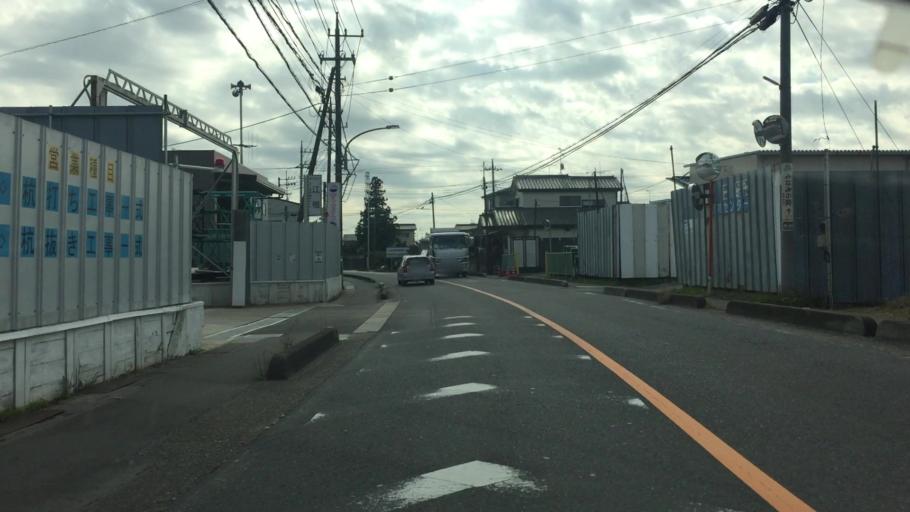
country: JP
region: Saitama
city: Yoshikawa
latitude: 35.8714
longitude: 139.8642
